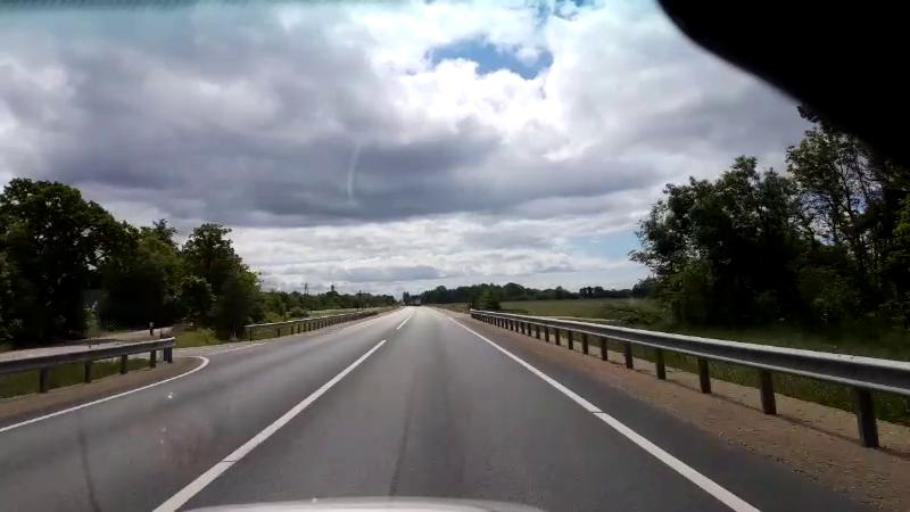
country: LV
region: Salacgrivas
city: Salacgriva
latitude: 57.7075
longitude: 24.3686
